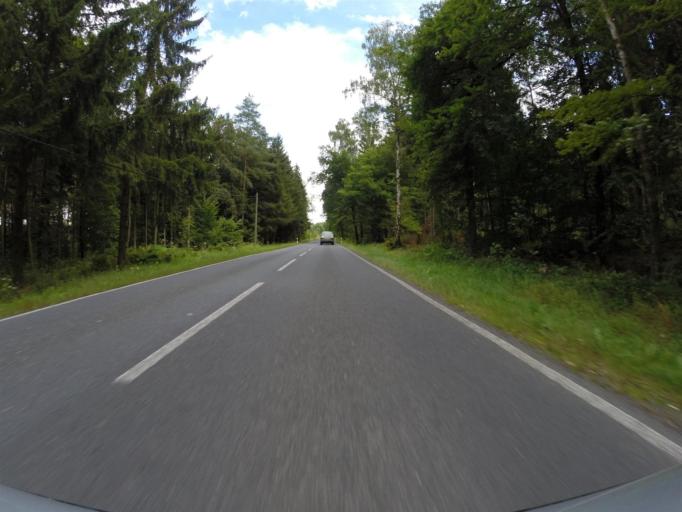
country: DE
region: Thuringia
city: Albersdorf
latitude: 50.8947
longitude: 11.7655
